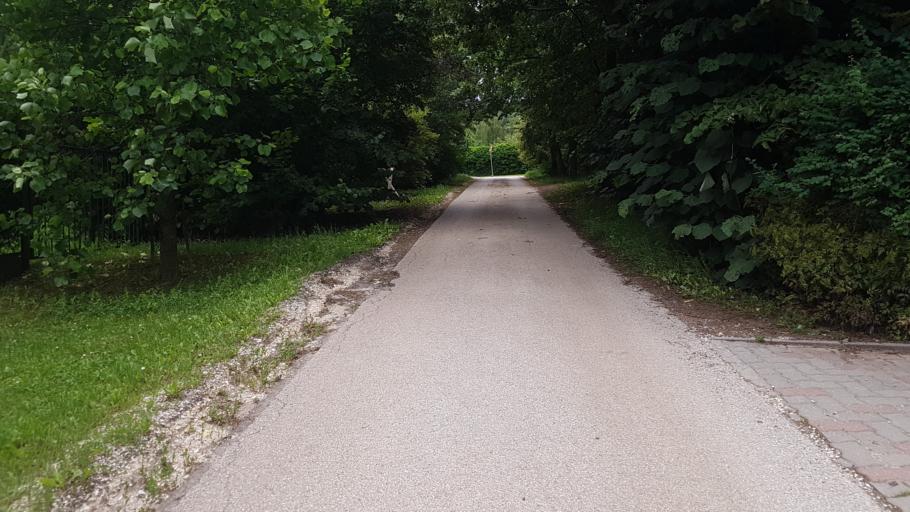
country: HU
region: Pest
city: Urom
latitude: 47.6137
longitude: 19.0163
